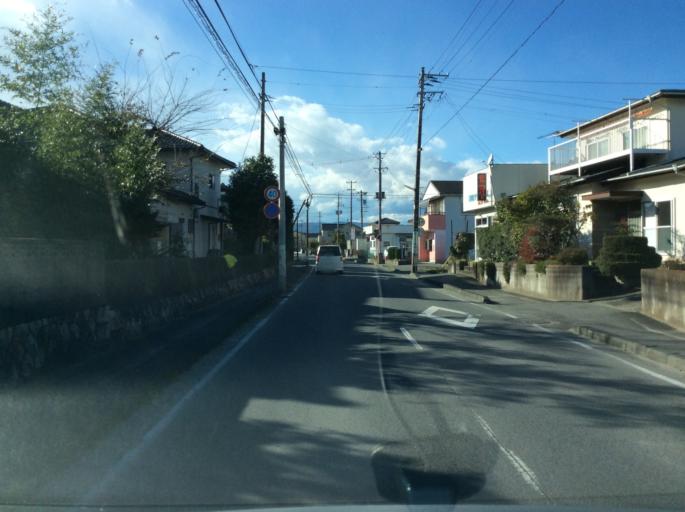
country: JP
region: Fukushima
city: Iwaki
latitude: 37.0630
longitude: 140.9290
